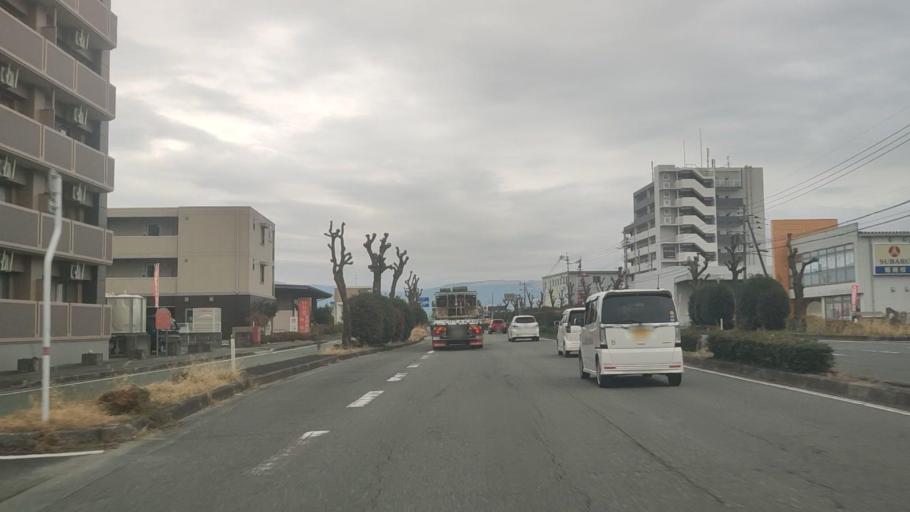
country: JP
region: Kumamoto
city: Ozu
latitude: 32.8633
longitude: 130.8238
